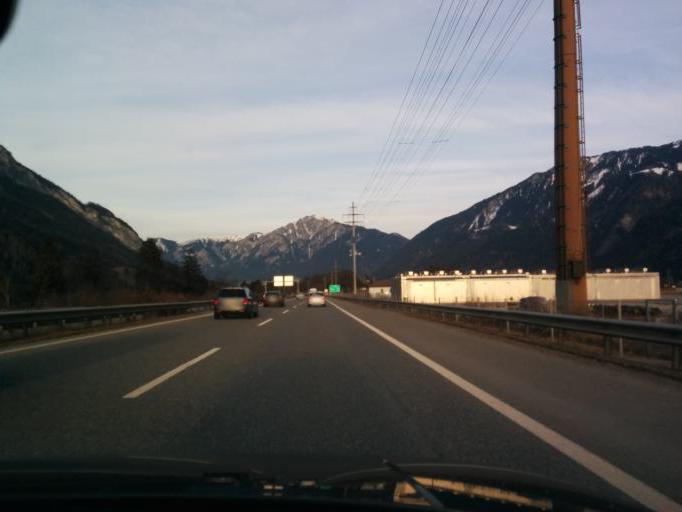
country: CH
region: Grisons
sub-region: Imboden District
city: Tamins
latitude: 46.8310
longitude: 9.4247
